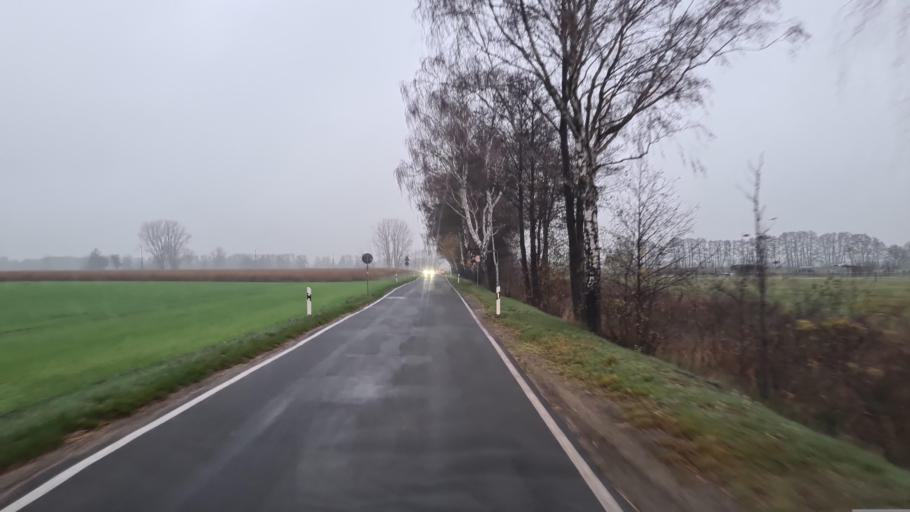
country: DE
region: Brandenburg
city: Beelitz
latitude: 52.2403
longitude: 13.0092
